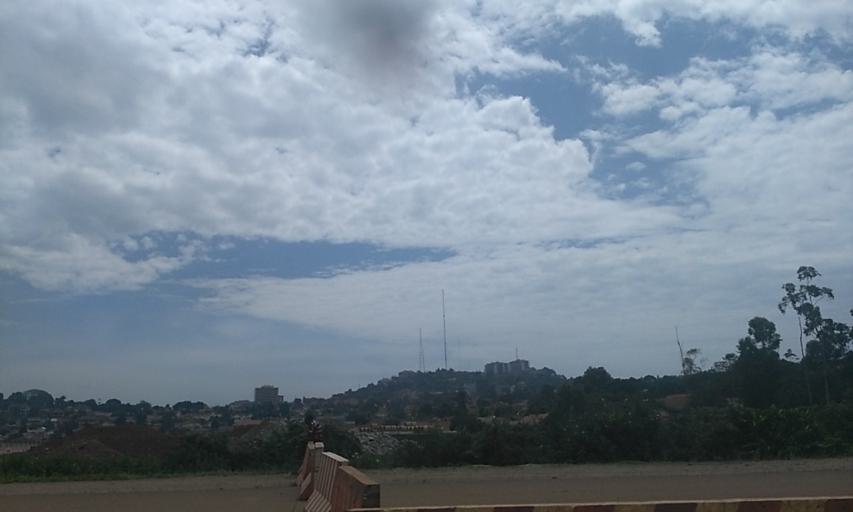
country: UG
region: Central Region
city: Kampala Central Division
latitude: 0.3593
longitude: 32.6006
